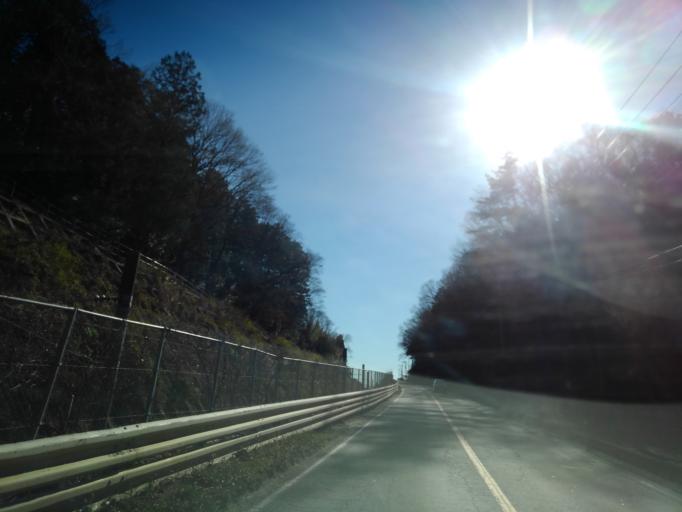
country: JP
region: Saitama
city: Hanno
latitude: 35.8192
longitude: 139.3244
